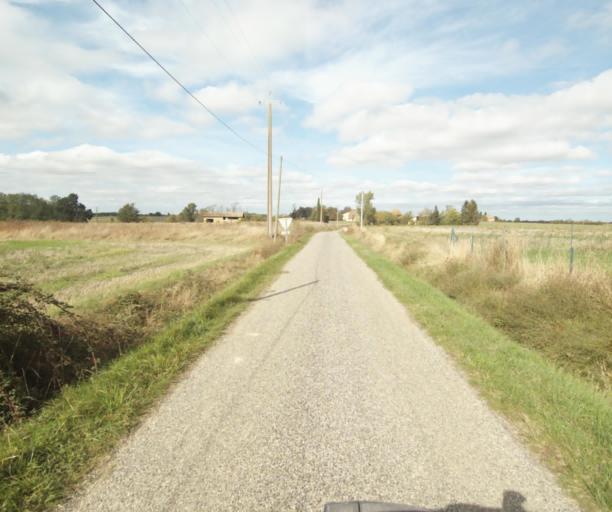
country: FR
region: Midi-Pyrenees
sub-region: Departement du Tarn-et-Garonne
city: Saint-Porquier
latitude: 43.9473
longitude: 1.1501
